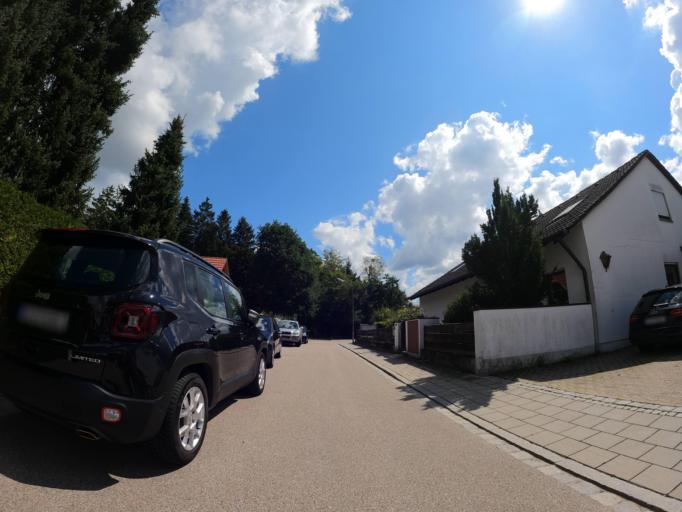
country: DE
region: Bavaria
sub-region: Upper Bavaria
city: Brunnthal
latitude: 48.0339
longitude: 11.6688
